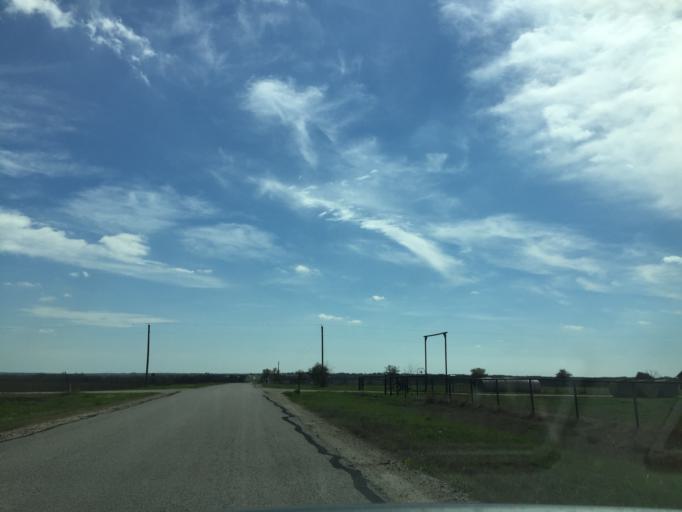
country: US
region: Texas
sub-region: Milam County
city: Thorndale
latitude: 30.5494
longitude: -97.2968
